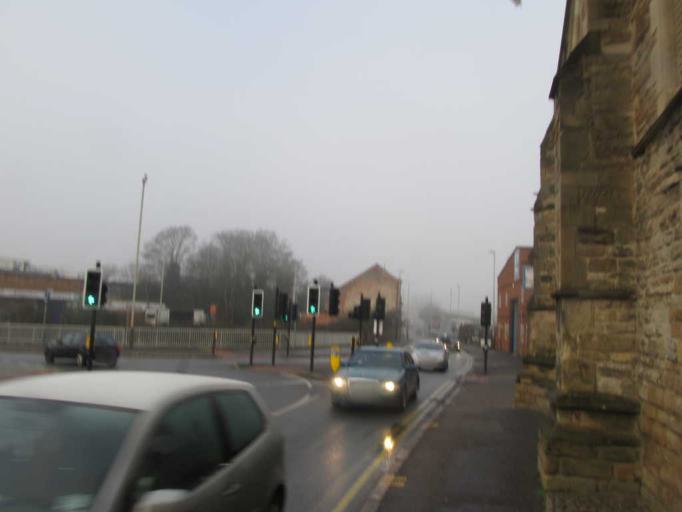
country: GB
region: England
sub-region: City of Leicester
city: Leicester
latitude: 52.6381
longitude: -1.1405
